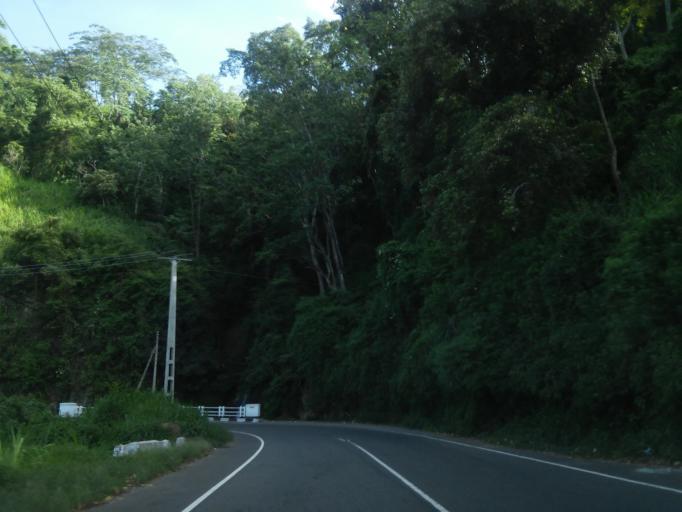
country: LK
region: Uva
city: Haputale
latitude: 6.7651
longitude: 80.8976
